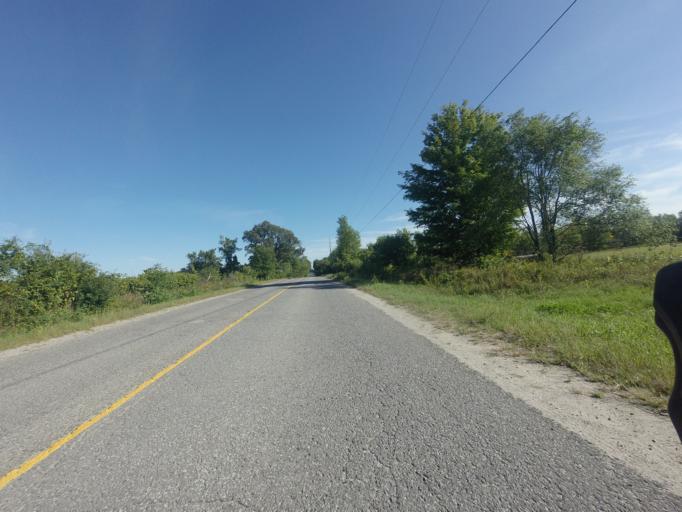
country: CA
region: Ontario
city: Perth
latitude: 44.9263
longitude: -76.3638
